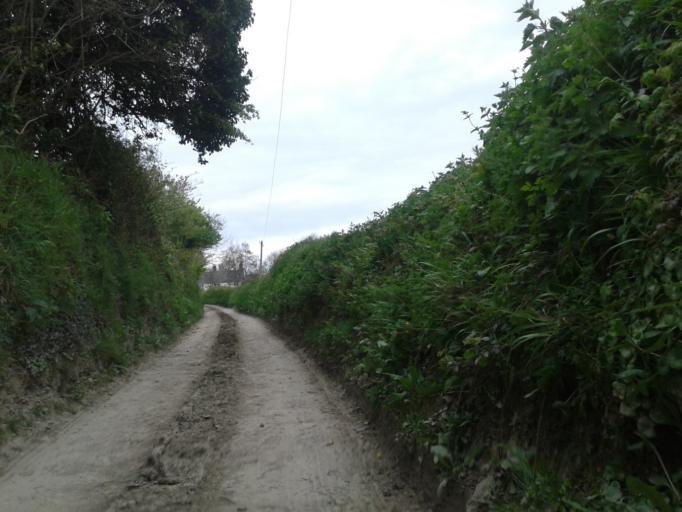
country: GB
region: England
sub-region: Devon
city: Braunton
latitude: 51.1340
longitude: -4.2170
